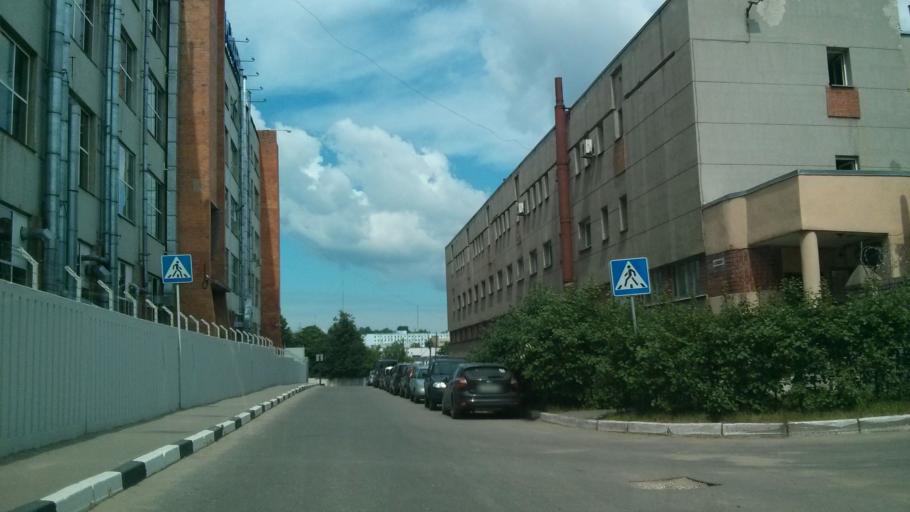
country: RU
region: Nizjnij Novgorod
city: Nizhniy Novgorod
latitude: 56.3022
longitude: 44.0174
